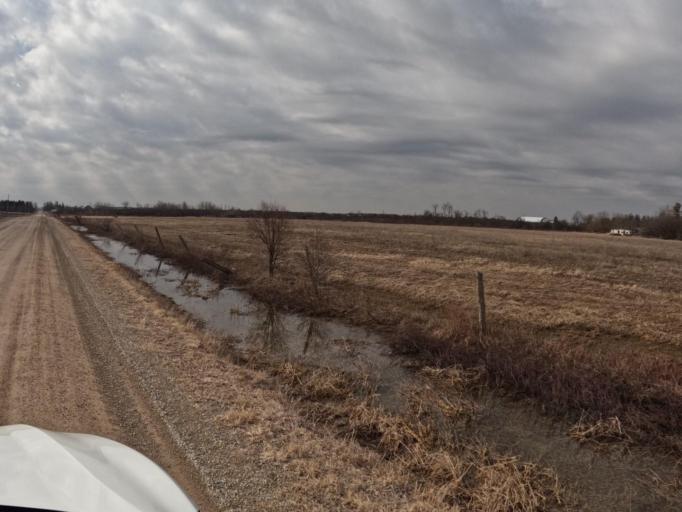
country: CA
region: Ontario
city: Orangeville
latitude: 43.9206
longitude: -80.2180
